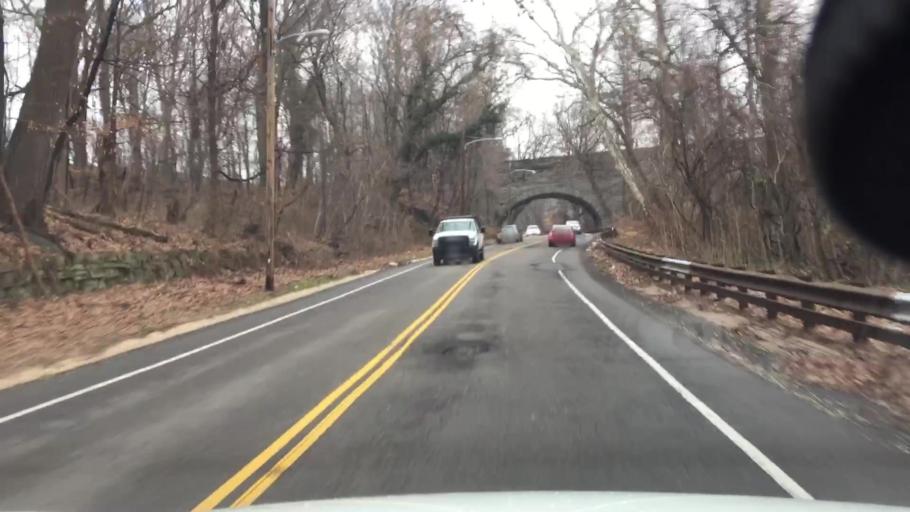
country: US
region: Pennsylvania
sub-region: Montgomery County
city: Wyndmoor
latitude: 40.0682
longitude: -75.1944
